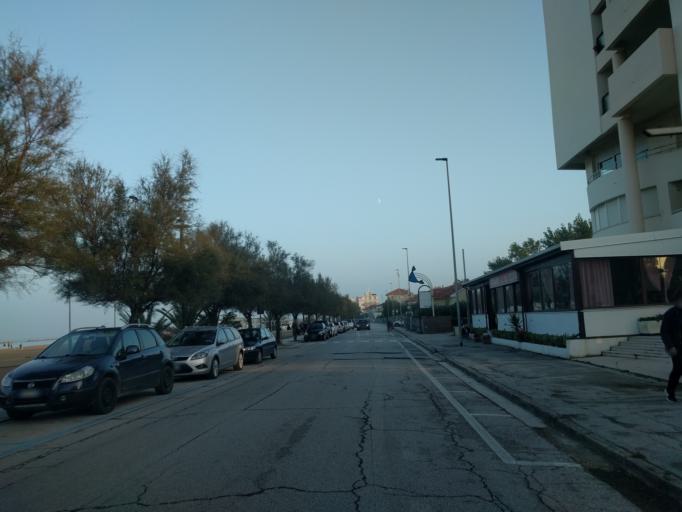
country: IT
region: The Marches
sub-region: Provincia di Ancona
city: Senigallia
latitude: 43.7259
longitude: 13.2079
